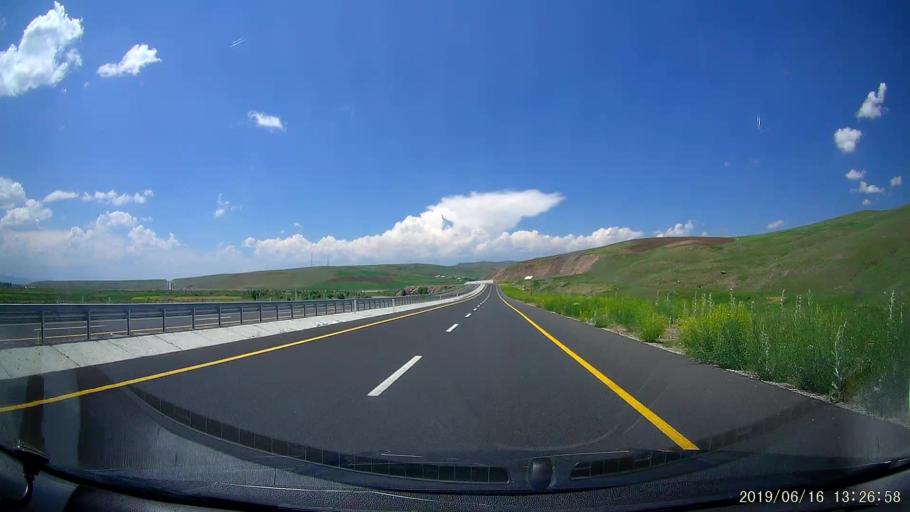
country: TR
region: Agri
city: Taslicay
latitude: 39.6648
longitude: 43.3176
